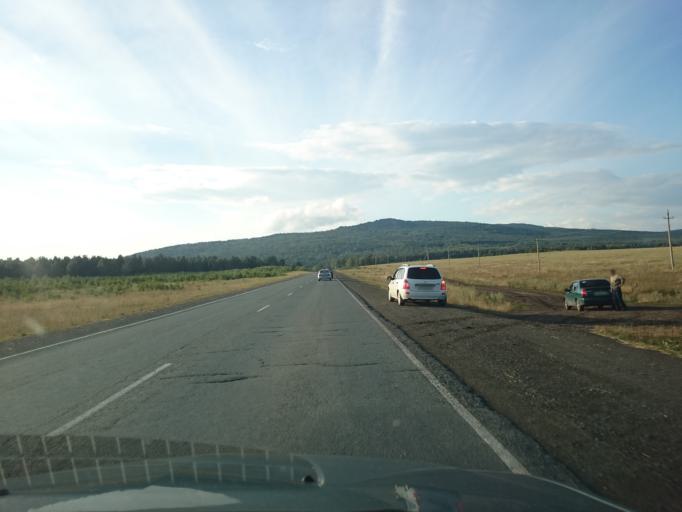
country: RU
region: Bashkortostan
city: Lomovka
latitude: 53.8891
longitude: 58.0963
